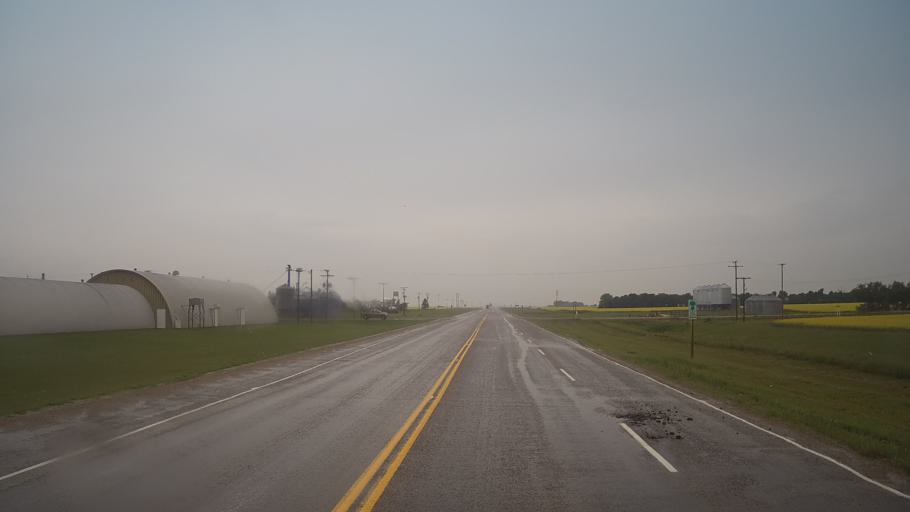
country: CA
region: Saskatchewan
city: Wilkie
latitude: 52.2020
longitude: -108.4527
